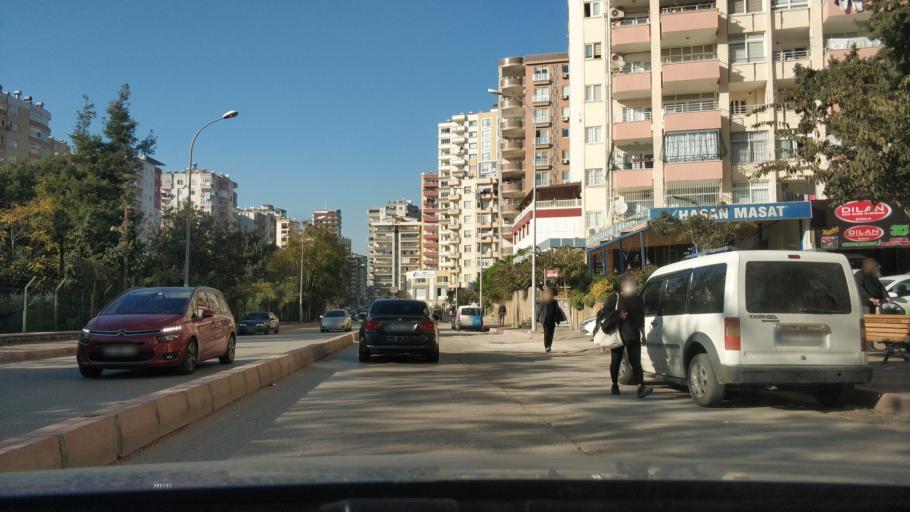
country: TR
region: Adana
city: Seyhan
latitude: 37.0506
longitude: 35.2792
